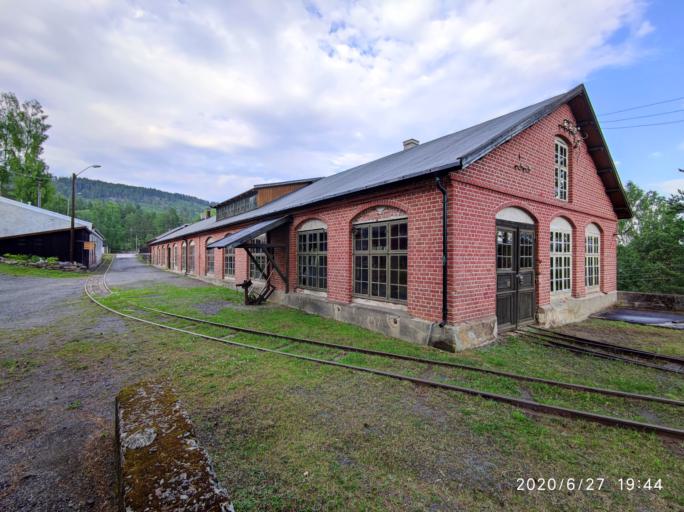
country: NO
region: Buskerud
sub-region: Kongsberg
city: Kongsberg
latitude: 59.6299
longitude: 9.5994
